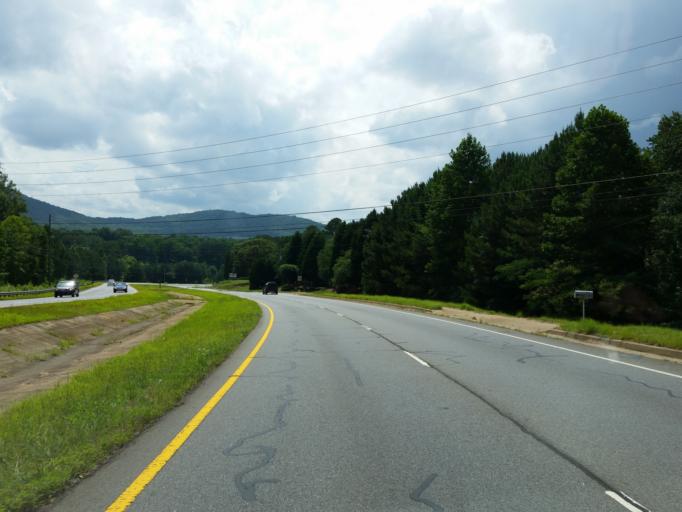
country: US
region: Georgia
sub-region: Cherokee County
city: Woodstock
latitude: 34.0777
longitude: -84.4339
